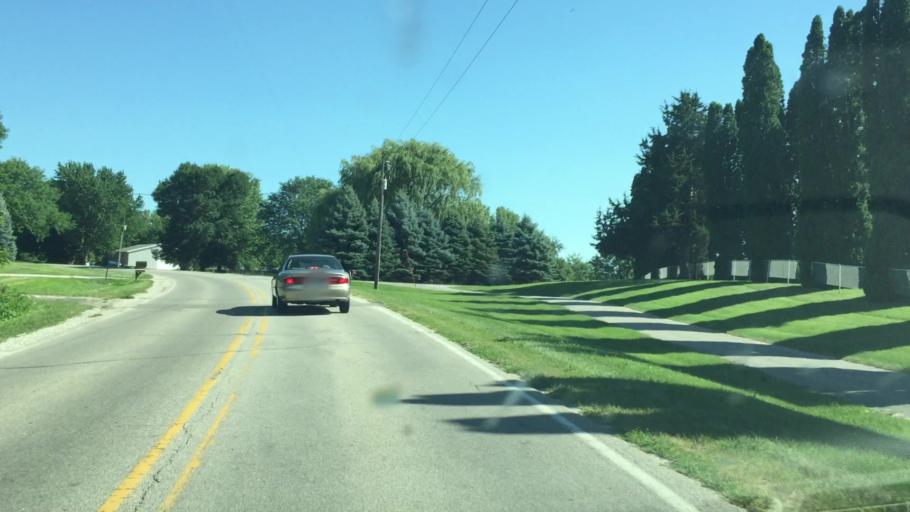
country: US
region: Iowa
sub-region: Linn County
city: Ely
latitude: 41.8432
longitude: -91.6461
